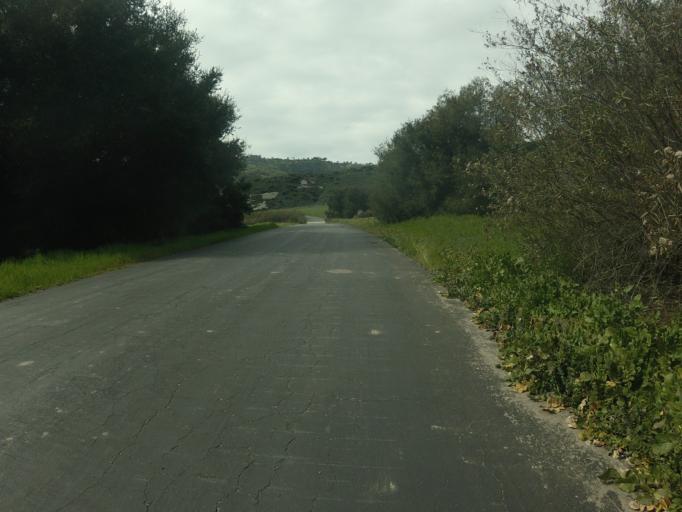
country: US
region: California
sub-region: Orange County
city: Aliso Viejo
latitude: 33.5439
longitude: -117.7312
